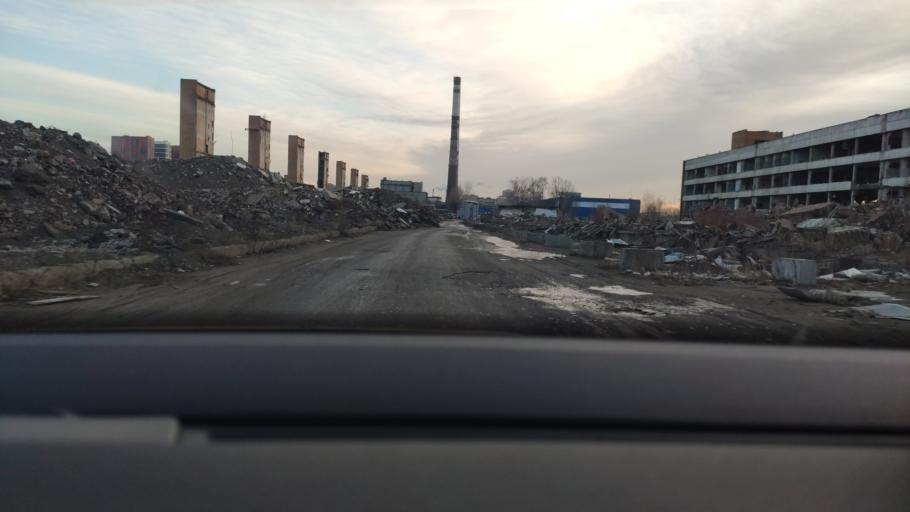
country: RU
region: Moskovskaya
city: Kozhukhovo
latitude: 55.6914
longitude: 37.6442
